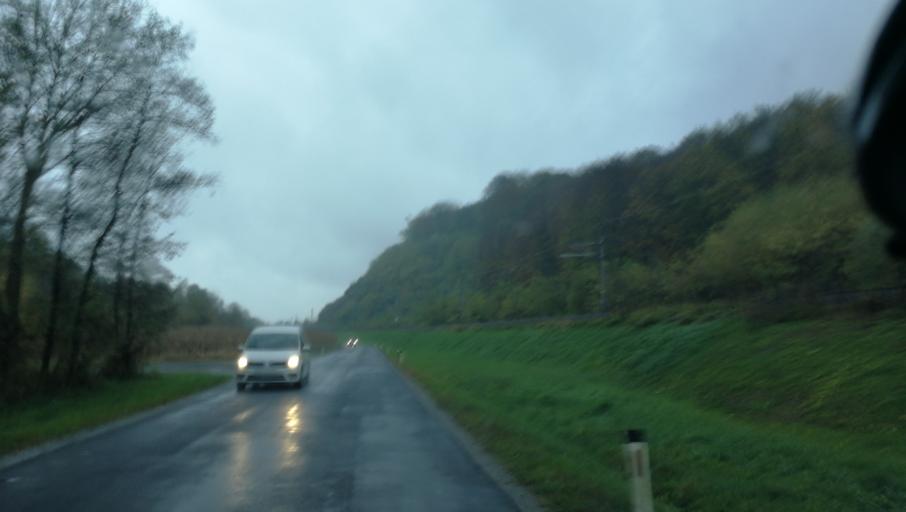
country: AT
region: Styria
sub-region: Politischer Bezirk Leibnitz
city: Ehrenhausen
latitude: 46.7256
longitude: 15.5935
